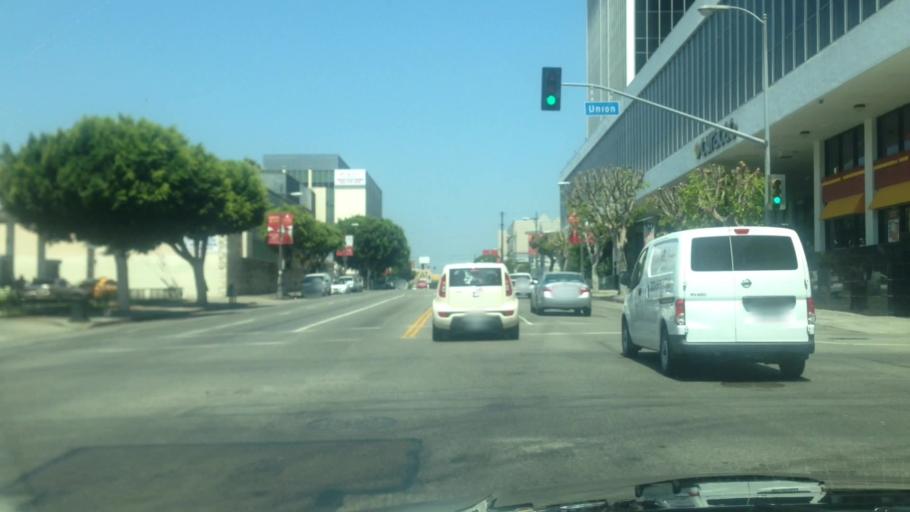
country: US
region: California
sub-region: Los Angeles County
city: Los Angeles
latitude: 34.0492
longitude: -118.2741
